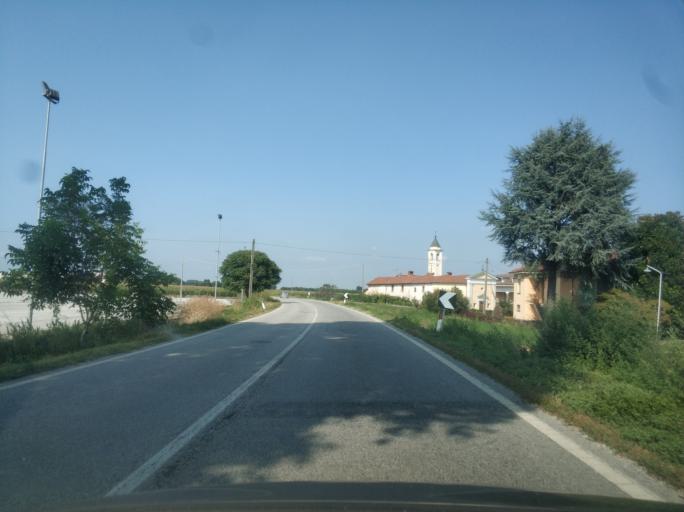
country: IT
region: Piedmont
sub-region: Provincia di Cuneo
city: Centallo
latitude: 44.5158
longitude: 7.5973
